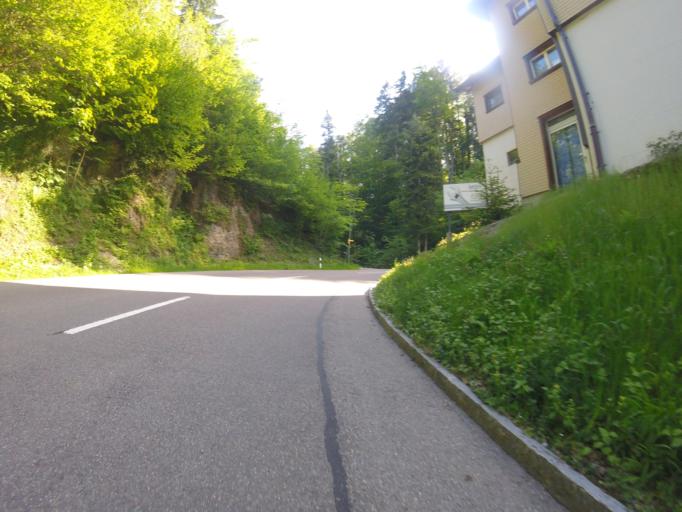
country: CH
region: Saint Gallen
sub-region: Wahlkreis Toggenburg
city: Mogelsberg
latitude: 47.3632
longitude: 9.1439
